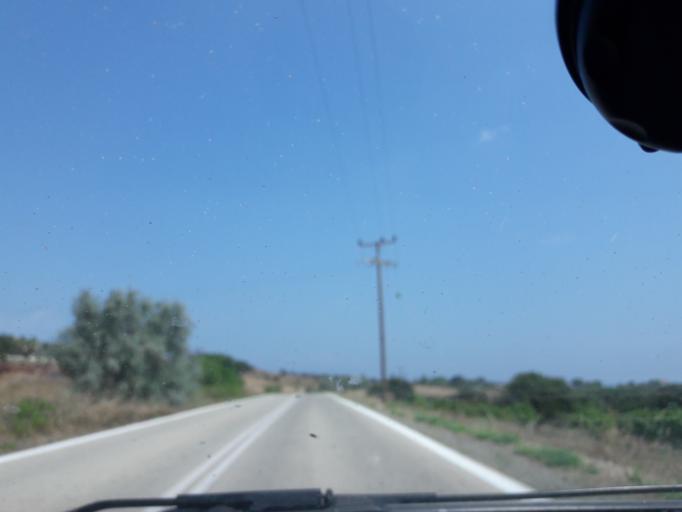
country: GR
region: North Aegean
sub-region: Nomos Lesvou
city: Myrina
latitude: 39.9252
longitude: 25.3217
